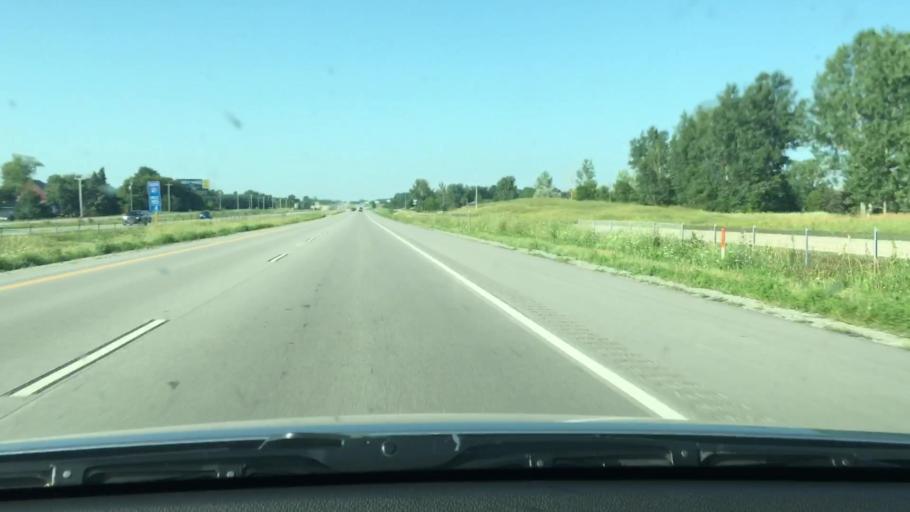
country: US
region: Wisconsin
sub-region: Brown County
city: Wrightstown
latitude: 44.3636
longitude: -88.1808
